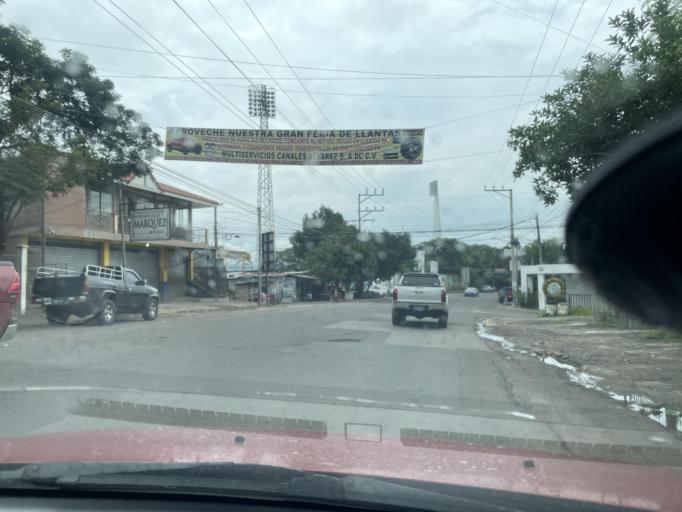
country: SV
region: La Union
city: Santa Rosa de Lima
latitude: 13.6311
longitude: -87.8912
